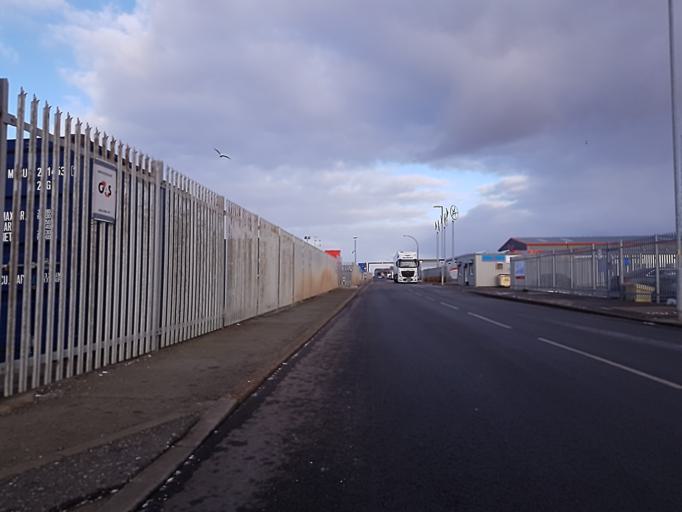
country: GB
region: England
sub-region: North East Lincolnshire
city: Grimsby
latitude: 53.5784
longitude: -0.0572
